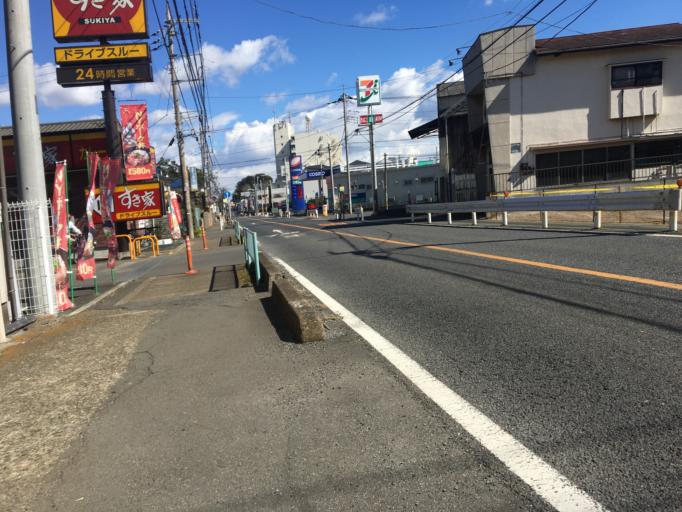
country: JP
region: Saitama
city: Shiki
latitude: 35.8133
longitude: 139.5535
